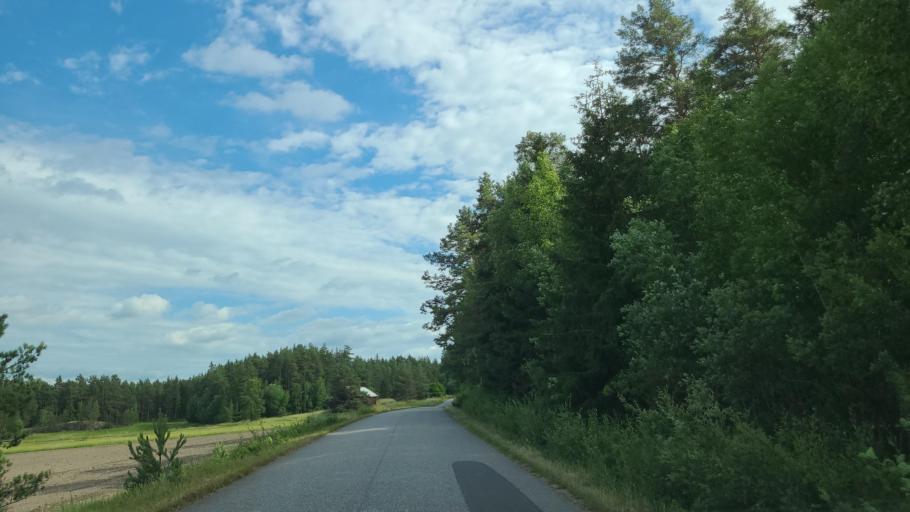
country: FI
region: Varsinais-Suomi
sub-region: Turku
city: Rymaettylae
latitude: 60.3060
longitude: 21.9406
